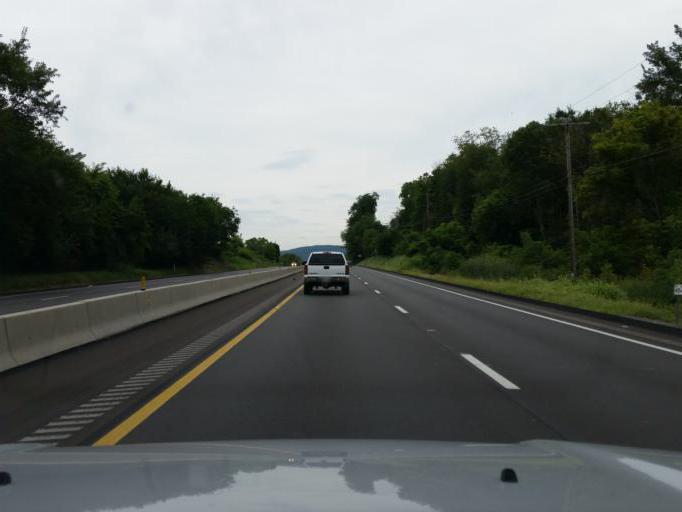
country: US
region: Pennsylvania
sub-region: Westmoreland County
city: Lawson Heights
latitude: 40.2831
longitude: -79.4193
